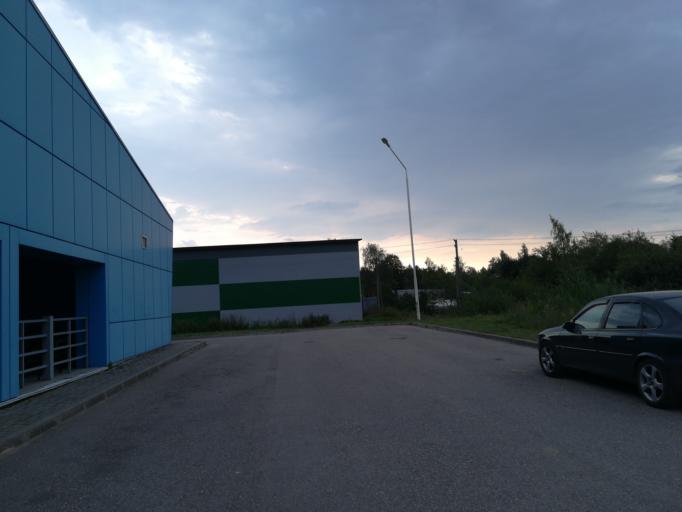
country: RU
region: Pskov
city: Opochka
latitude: 56.7090
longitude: 28.6921
